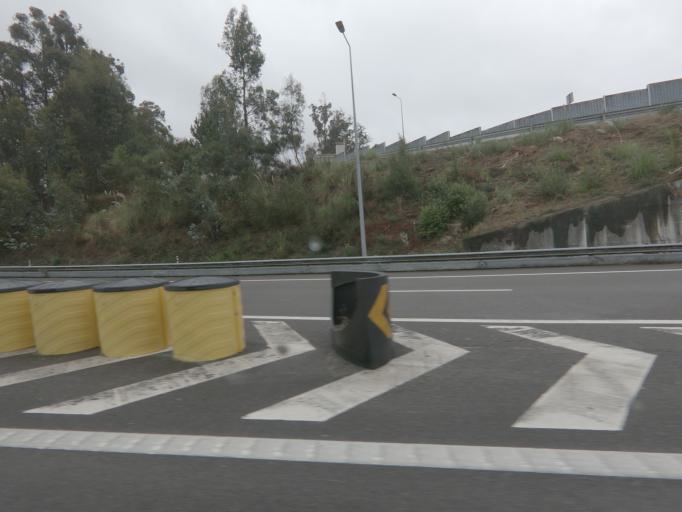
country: PT
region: Porto
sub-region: Matosinhos
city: Sao Mamede de Infesta
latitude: 41.1968
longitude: -8.5922
